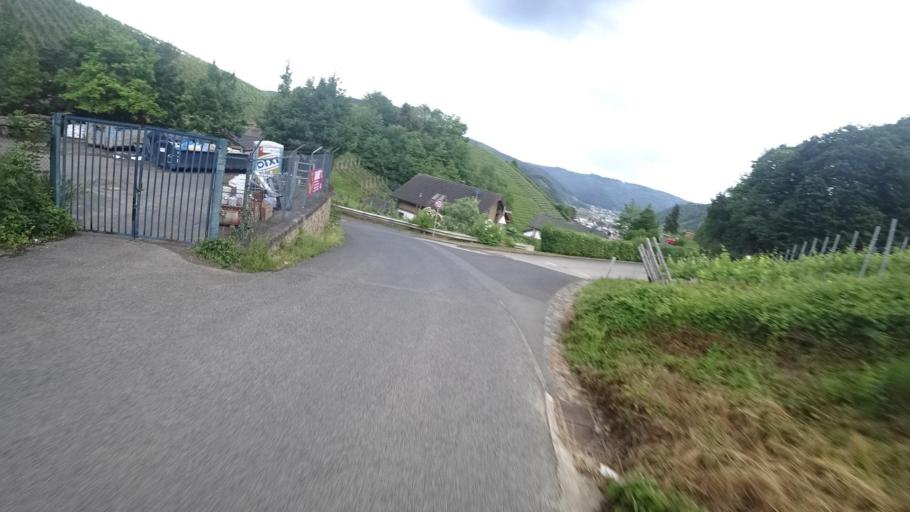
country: DE
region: Rheinland-Pfalz
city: Dernau
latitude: 50.5392
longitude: 7.0420
